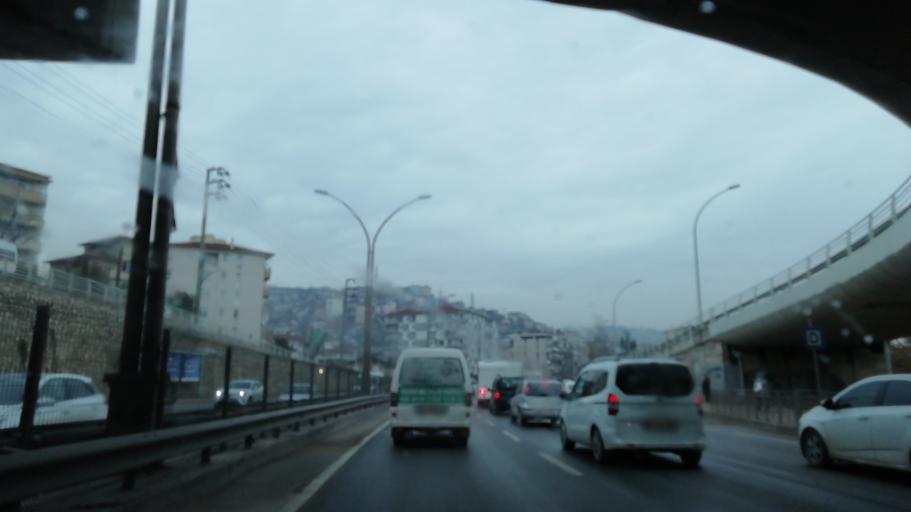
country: TR
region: Kocaeli
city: Izmit
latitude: 40.7660
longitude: 29.8993
